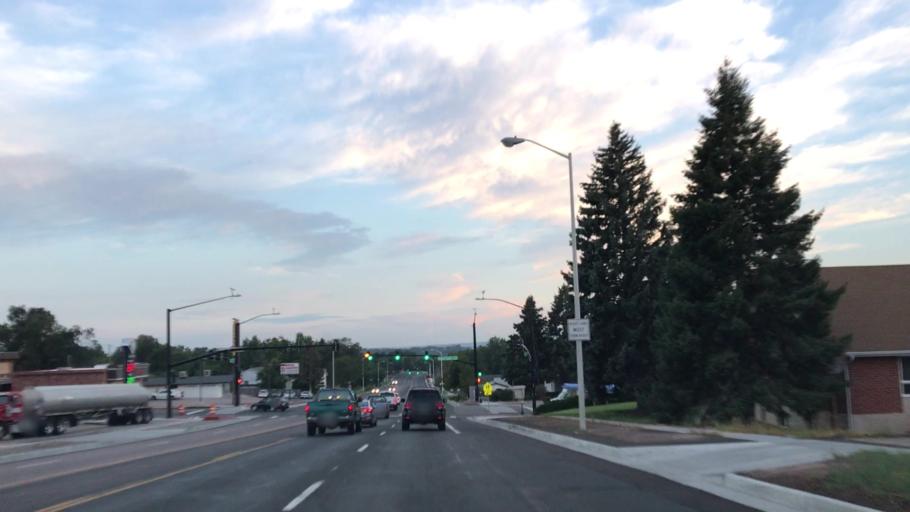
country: US
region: Colorado
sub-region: El Paso County
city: Colorado Springs
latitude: 38.8335
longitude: -104.7760
